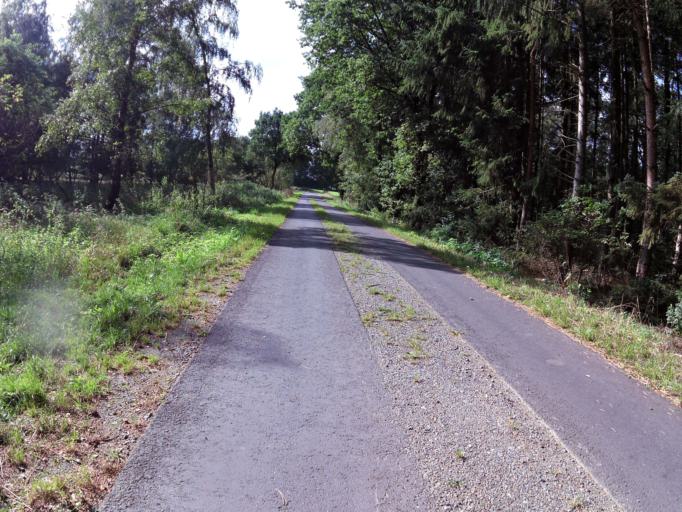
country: DE
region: Lower Saxony
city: Sandbostel
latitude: 53.4462
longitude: 9.1242
